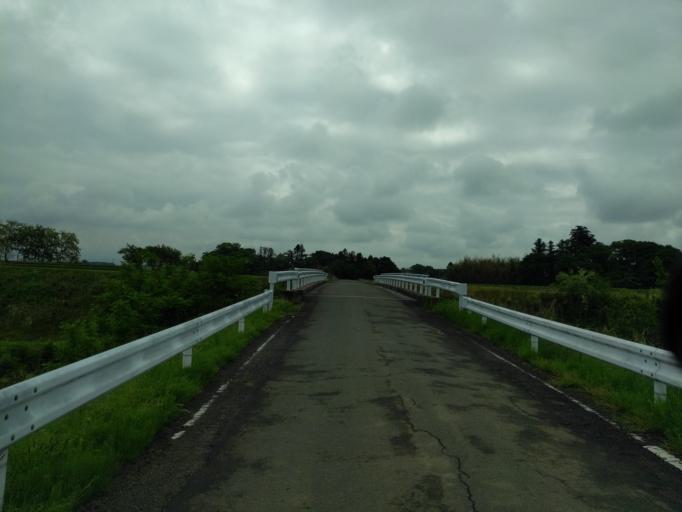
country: JP
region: Fukushima
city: Koriyama
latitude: 37.3497
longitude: 140.2805
